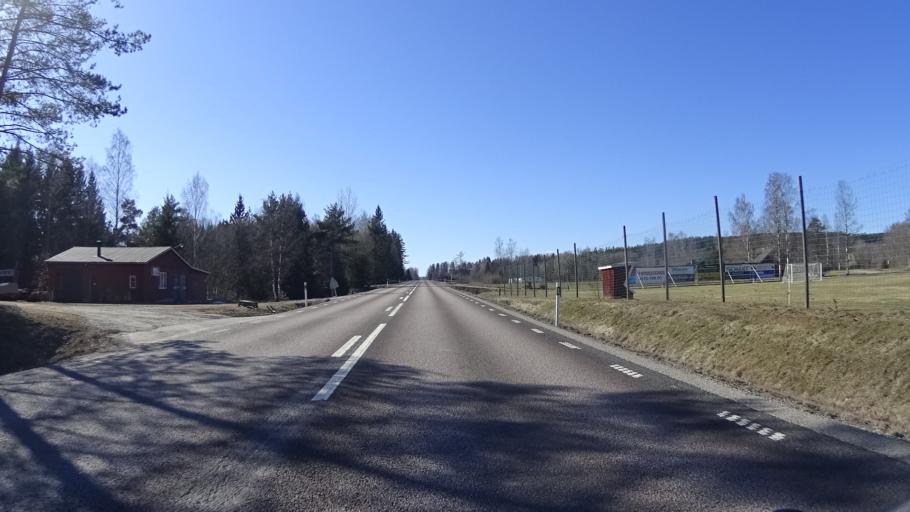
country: SE
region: Vaermland
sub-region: Arvika Kommun
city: Arvika
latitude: 59.6658
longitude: 12.8609
